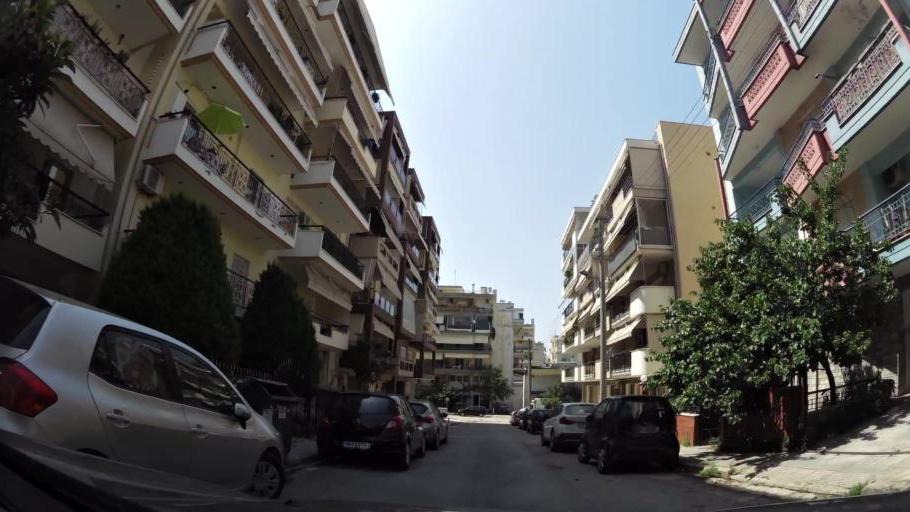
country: GR
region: Central Macedonia
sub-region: Nomos Thessalonikis
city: Evosmos
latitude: 40.6749
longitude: 22.9187
